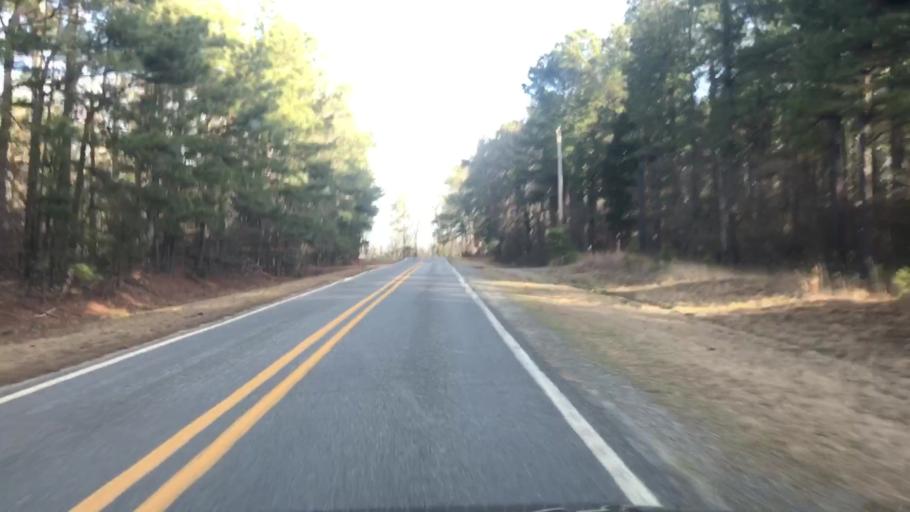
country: US
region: Arkansas
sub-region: Garland County
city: Rockwell
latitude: 34.4852
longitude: -93.2733
